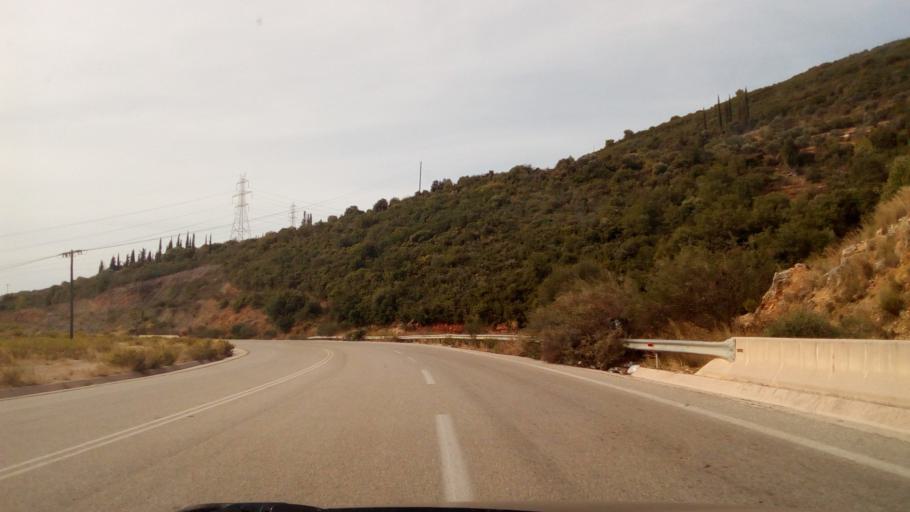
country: GR
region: West Greece
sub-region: Nomos Aitolias kai Akarnanias
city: Nafpaktos
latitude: 38.4065
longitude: 21.8373
